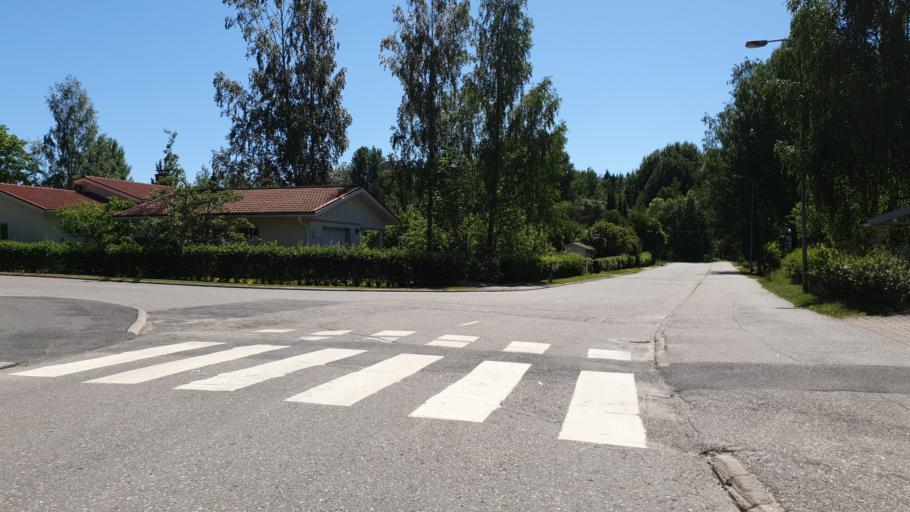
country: FI
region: Uusimaa
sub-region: Helsinki
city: Kilo
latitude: 60.2698
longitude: 24.8303
